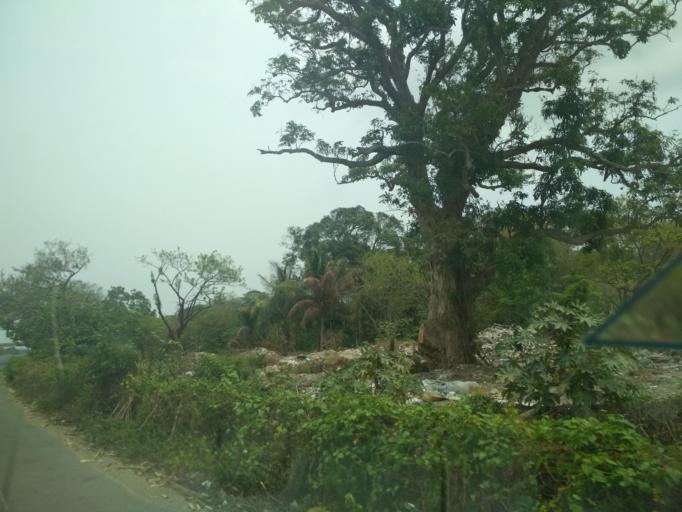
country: MX
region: Veracruz
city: Paso del Toro
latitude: 19.0356
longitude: -96.1516
